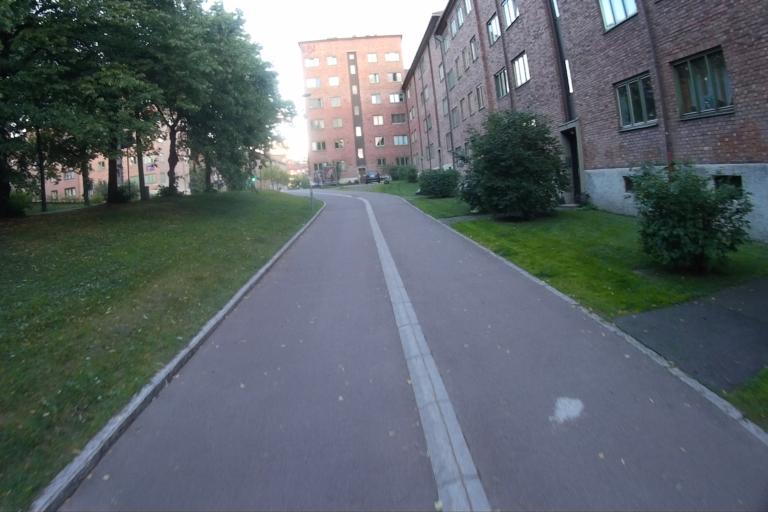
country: NO
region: Oslo
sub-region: Oslo
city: Oslo
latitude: 59.9277
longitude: 10.7725
